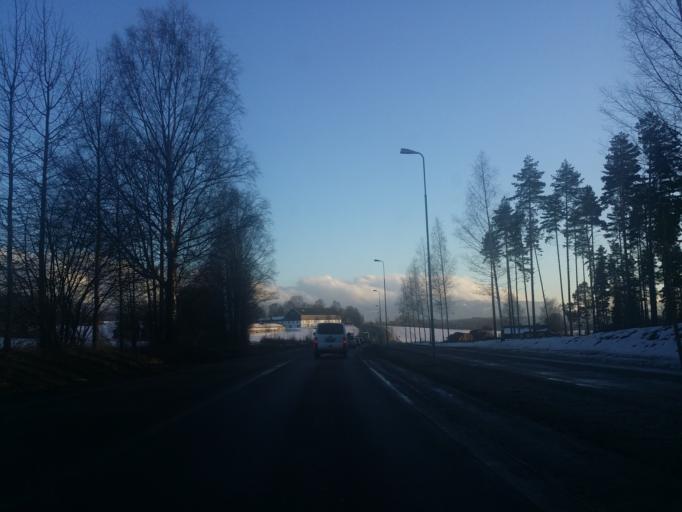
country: NO
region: Buskerud
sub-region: Ringerike
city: Honefoss
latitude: 60.1437
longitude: 10.2606
